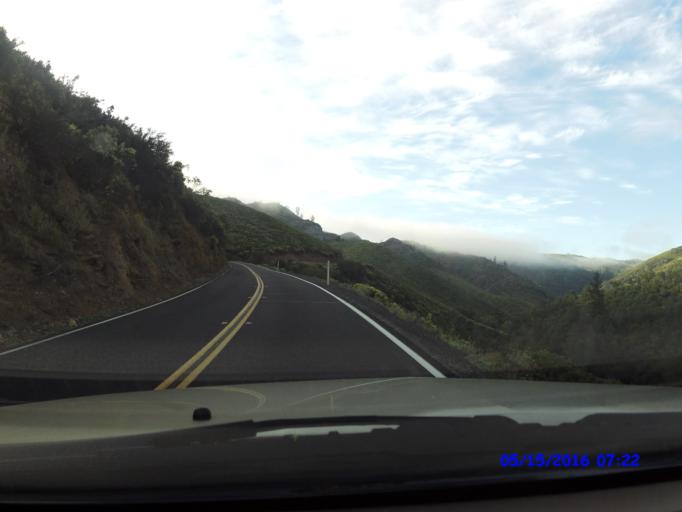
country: US
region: California
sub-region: Tuolumne County
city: Tuolumne City
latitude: 37.7733
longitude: -120.2662
